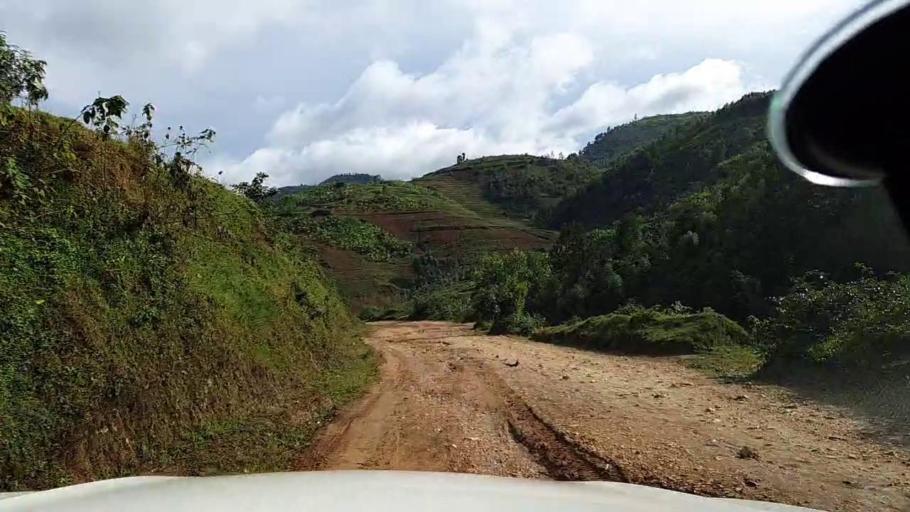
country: RW
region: Western Province
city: Kibuye
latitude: -2.1273
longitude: 29.4984
